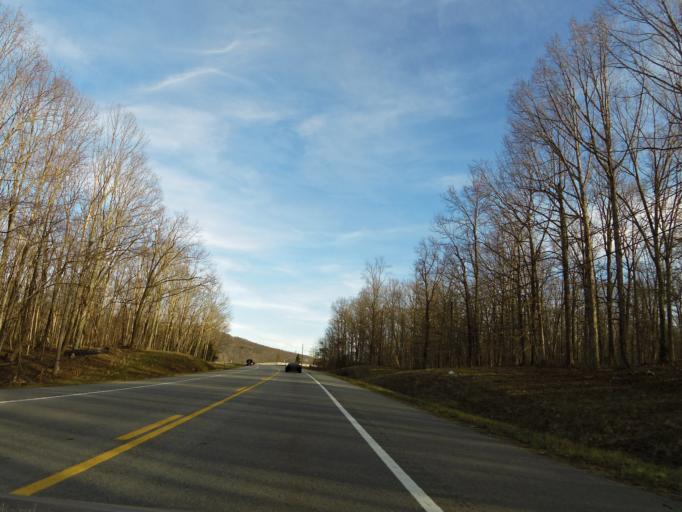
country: US
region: Tennessee
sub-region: White County
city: Sparta
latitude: 35.9234
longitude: -85.4139
